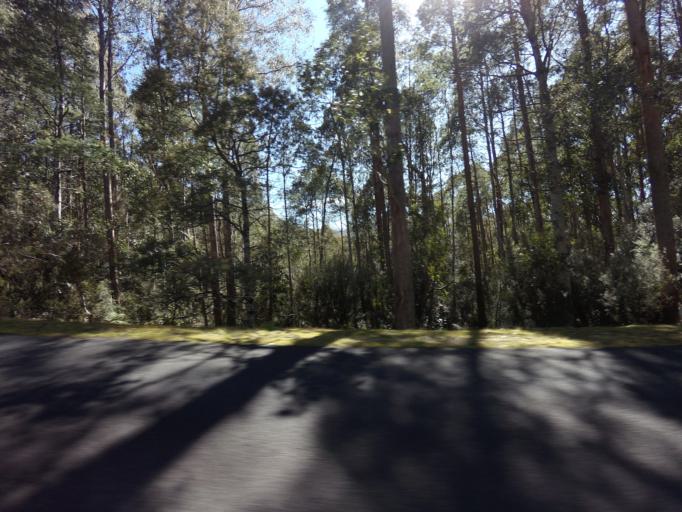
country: AU
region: Tasmania
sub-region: Derwent Valley
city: New Norfolk
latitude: -42.7303
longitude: 146.4687
